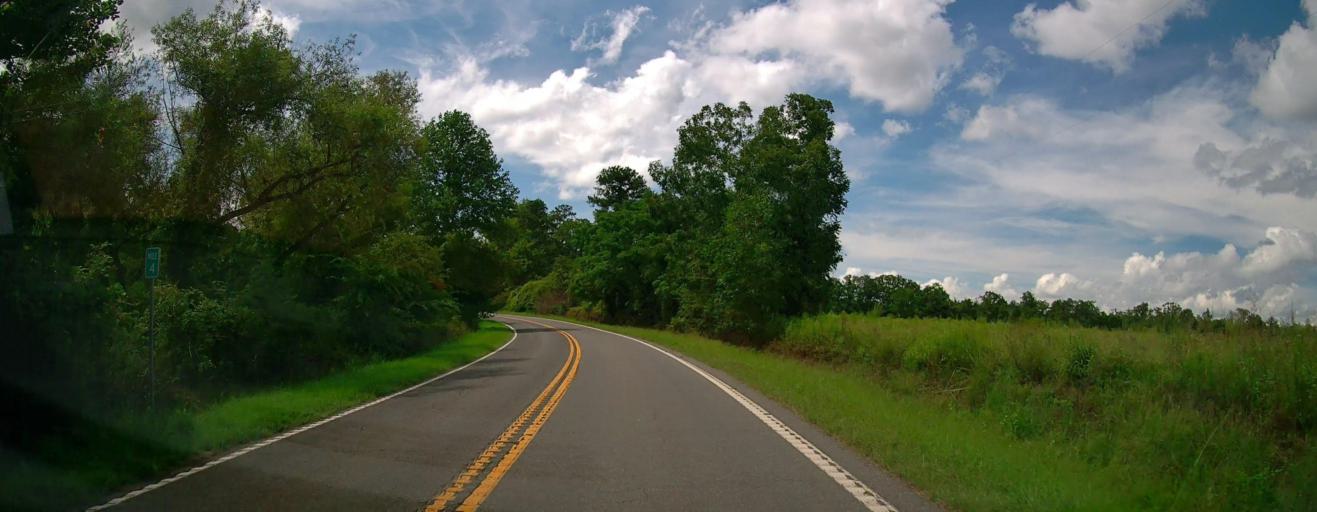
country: US
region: Georgia
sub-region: Taylor County
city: Reynolds
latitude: 32.4406
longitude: -84.1077
